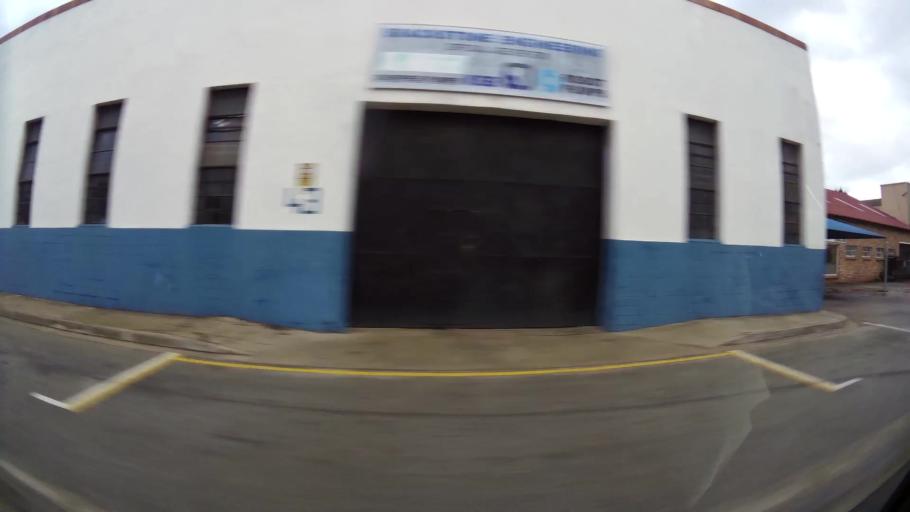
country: ZA
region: Eastern Cape
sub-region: Nelson Mandela Bay Metropolitan Municipality
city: Port Elizabeth
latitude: -33.9353
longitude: 25.6094
